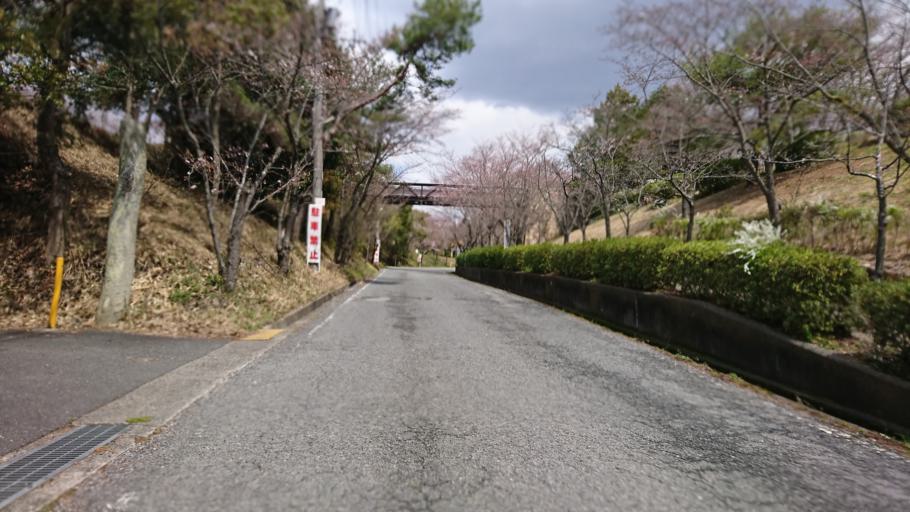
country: JP
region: Hyogo
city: Miki
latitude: 34.7721
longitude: 134.9480
